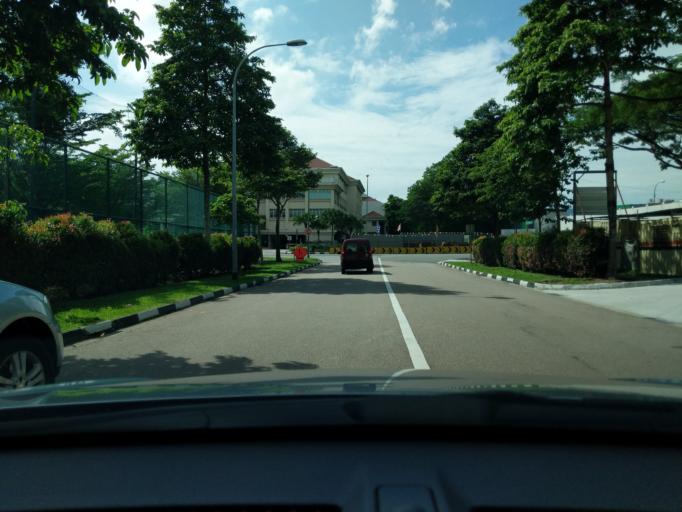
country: SG
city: Singapore
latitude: 1.2984
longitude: 103.8807
